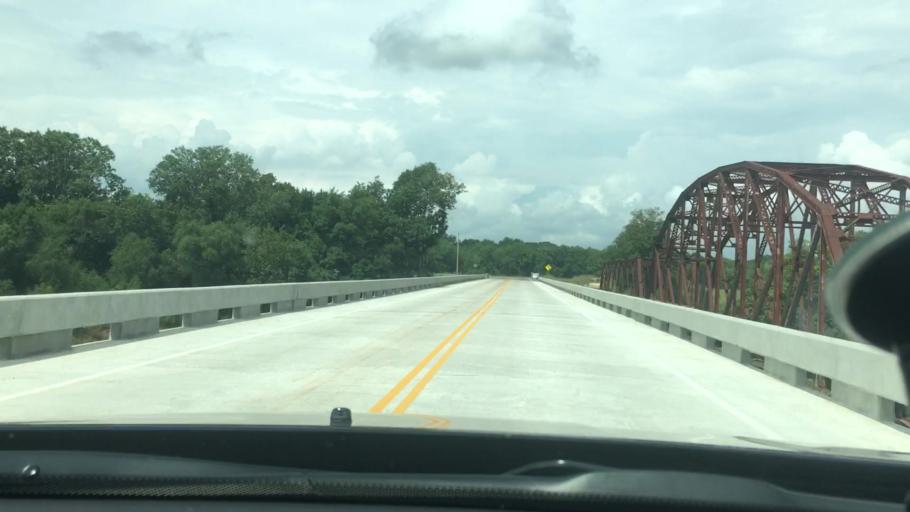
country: US
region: Oklahoma
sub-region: Carter County
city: Dickson
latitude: 34.2295
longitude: -96.9083
